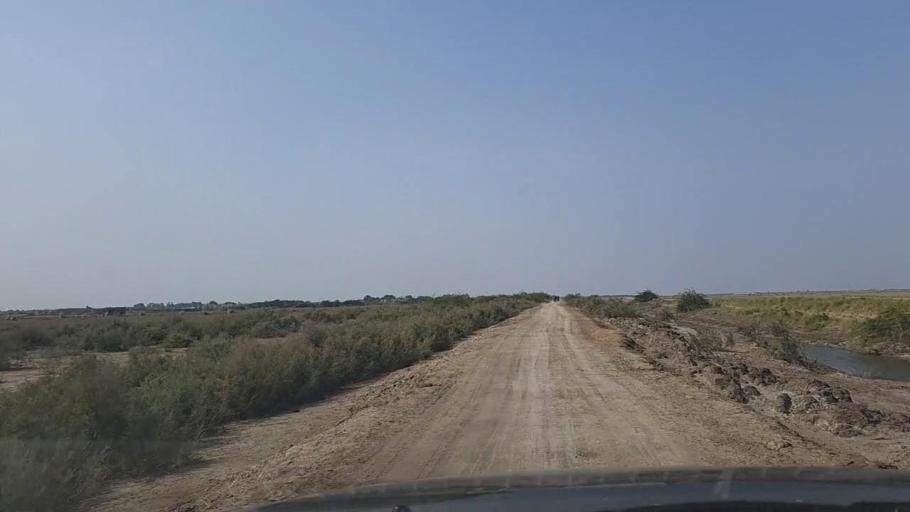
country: PK
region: Sindh
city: Gharo
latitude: 24.7046
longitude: 67.5797
